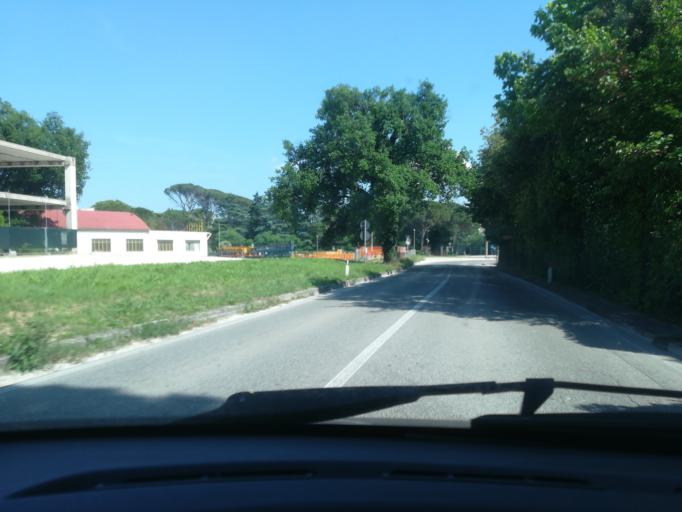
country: IT
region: The Marches
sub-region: Provincia di Macerata
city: Passo di Treia
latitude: 43.2892
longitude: 13.3329
